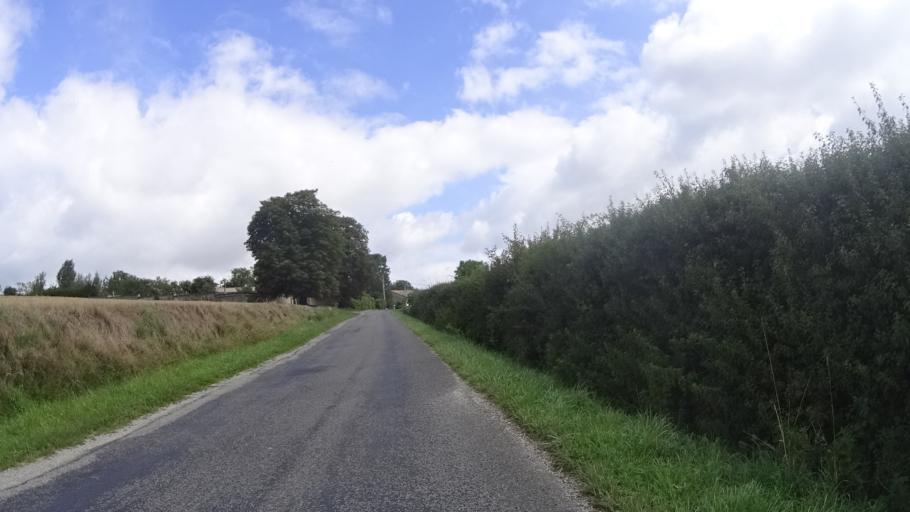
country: FR
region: Lorraine
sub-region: Departement de la Meuse
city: Ligny-en-Barrois
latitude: 48.7406
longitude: 5.3887
